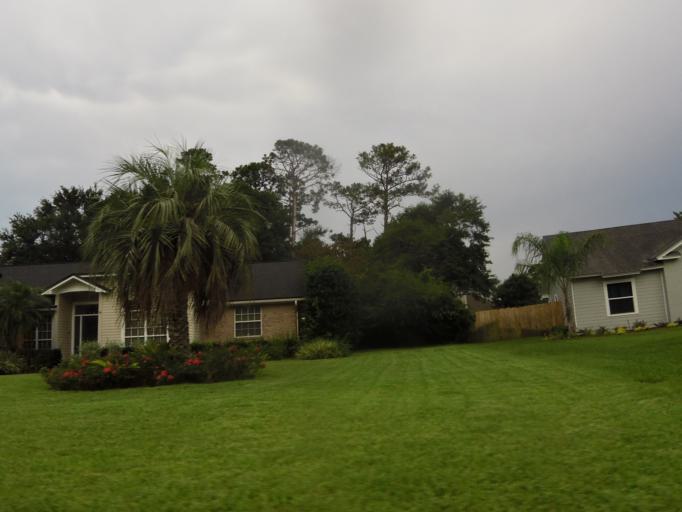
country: US
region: Florida
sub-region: Duval County
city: Jacksonville Beach
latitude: 30.2676
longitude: -81.4060
